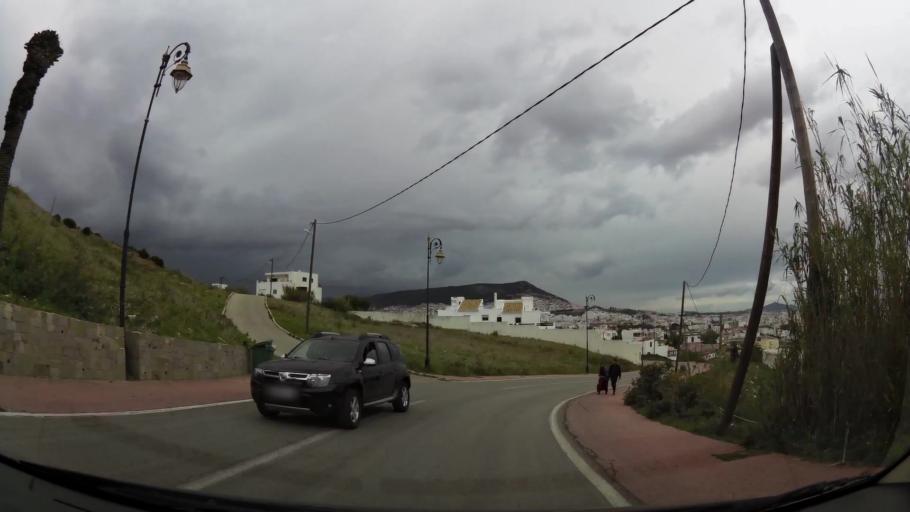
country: MA
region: Tanger-Tetouan
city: Tetouan
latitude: 35.5502
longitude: -5.3717
